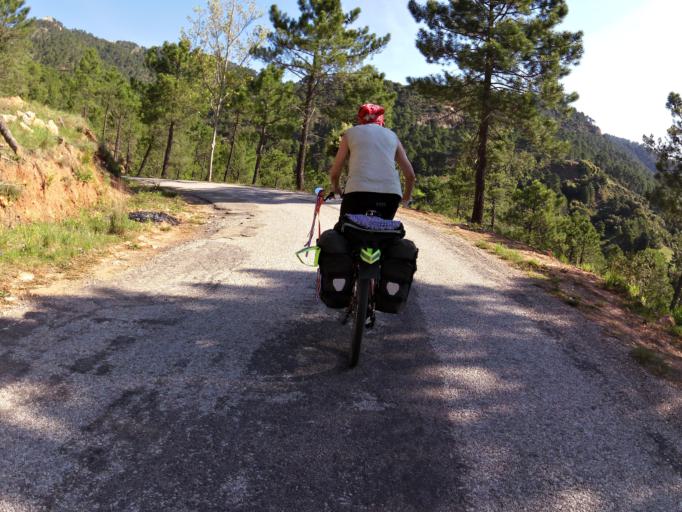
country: ES
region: Castille-La Mancha
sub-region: Provincia de Albacete
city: Riopar
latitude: 38.5203
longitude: -2.4551
